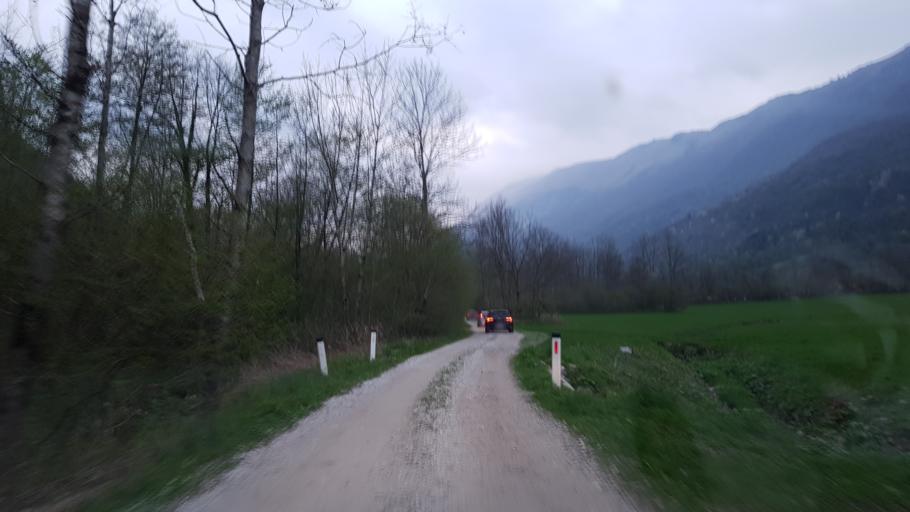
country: SI
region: Kobarid
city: Kobarid
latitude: 46.2415
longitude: 13.5302
